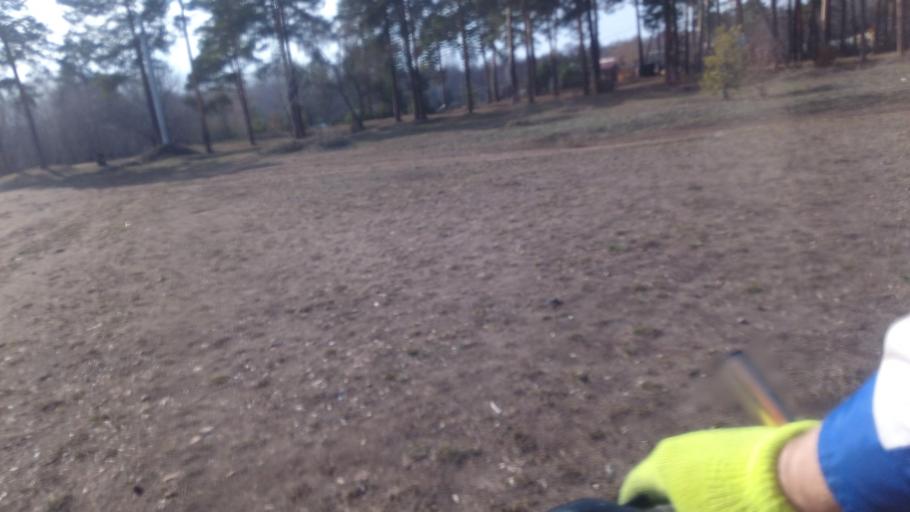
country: RU
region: Chelyabinsk
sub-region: Gorod Chelyabinsk
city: Chelyabinsk
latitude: 55.1539
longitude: 61.3360
